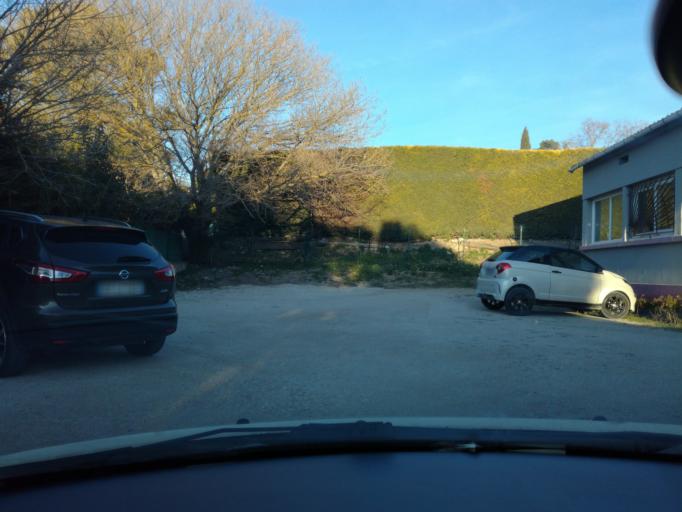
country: FR
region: Provence-Alpes-Cote d'Azur
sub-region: Departement des Bouches-du-Rhone
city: Plan-de-Cuques
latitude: 43.3305
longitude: 5.4617
